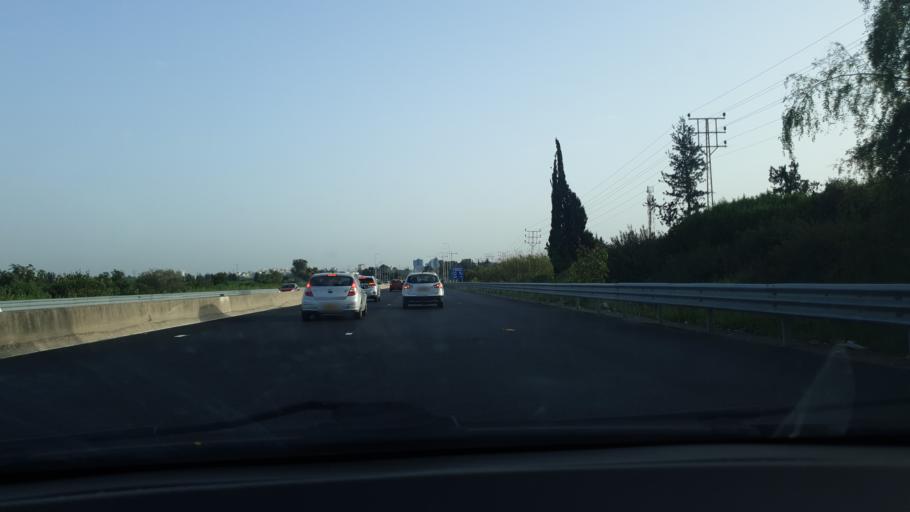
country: IL
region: Central District
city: Ra'anana
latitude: 32.2232
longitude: 34.8829
